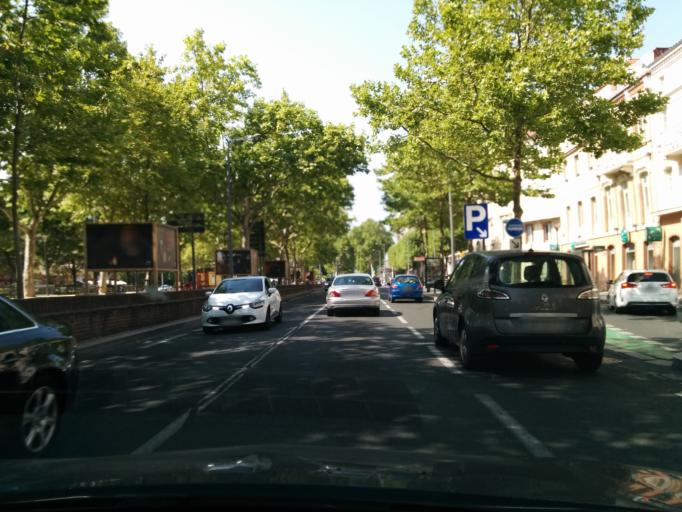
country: FR
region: Midi-Pyrenees
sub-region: Departement du Tarn
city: Albi
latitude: 43.9258
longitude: 2.1485
